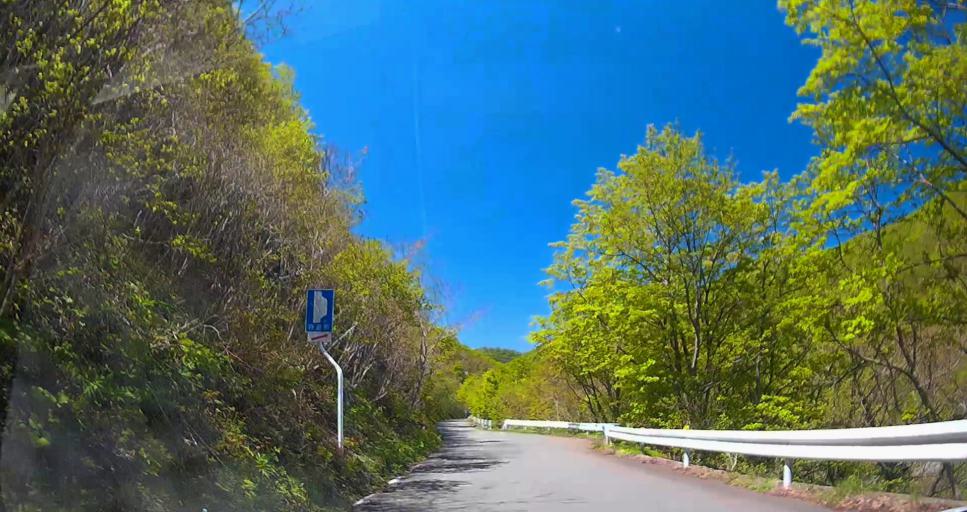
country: JP
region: Aomori
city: Mutsu
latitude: 41.3247
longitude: 140.8169
